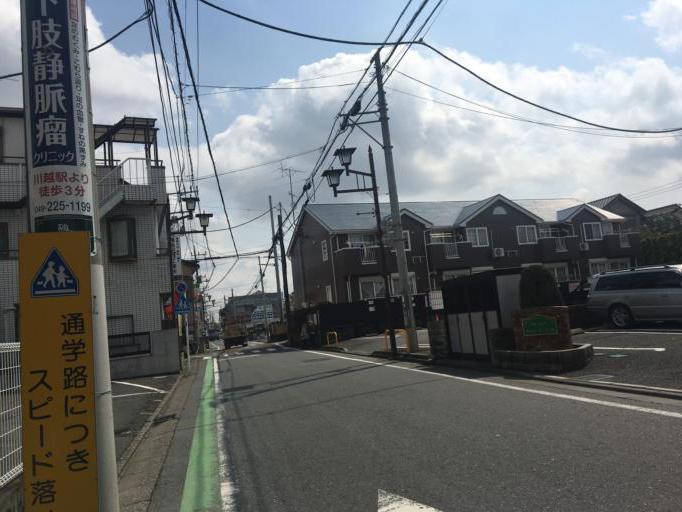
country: JP
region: Saitama
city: Kawagoe
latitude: 35.8903
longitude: 139.5002
